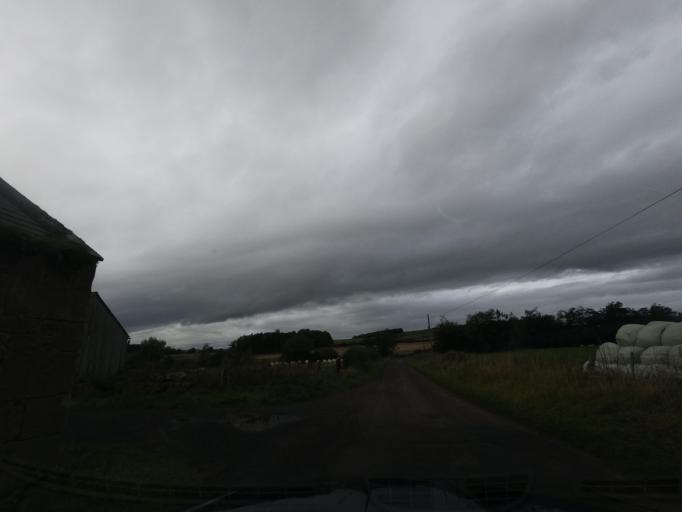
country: GB
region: England
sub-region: Northumberland
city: Ford
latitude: 55.5990
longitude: -2.0476
